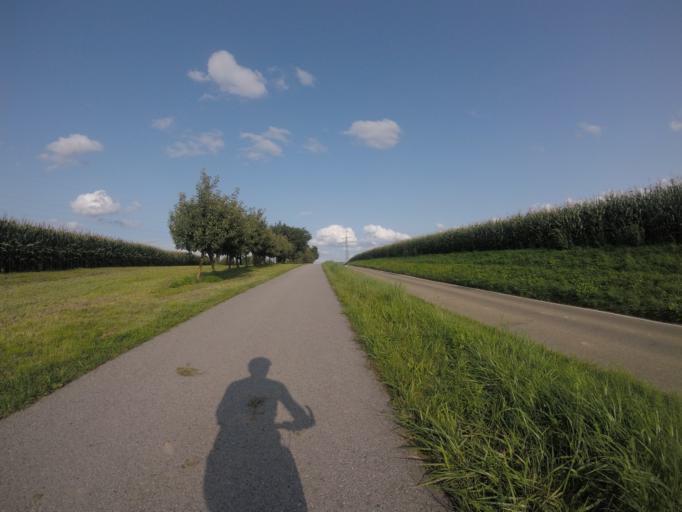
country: DE
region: Baden-Wuerttemberg
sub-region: Regierungsbezirk Stuttgart
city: Mittelschontal
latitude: 48.9489
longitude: 9.4031
